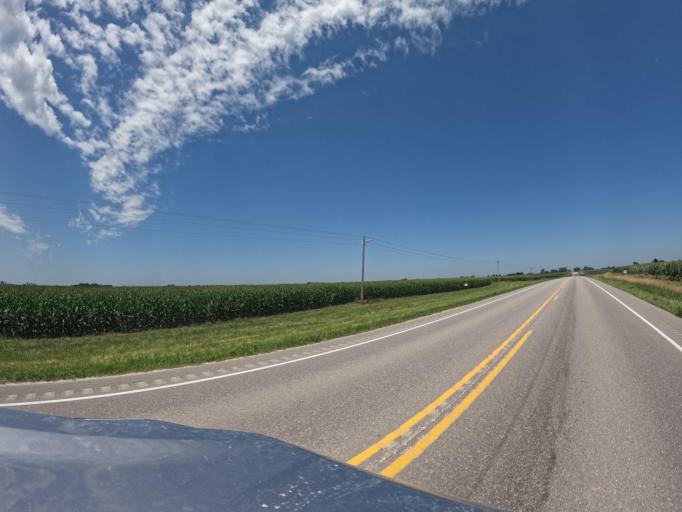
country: US
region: Iowa
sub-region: Keokuk County
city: Sigourney
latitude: 41.4165
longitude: -92.3546
